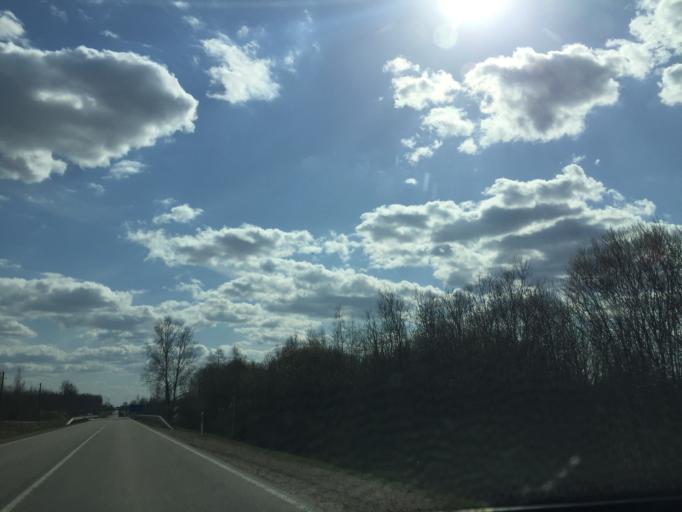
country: LV
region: Skriveri
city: Skriveri
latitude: 56.7368
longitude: 25.1640
